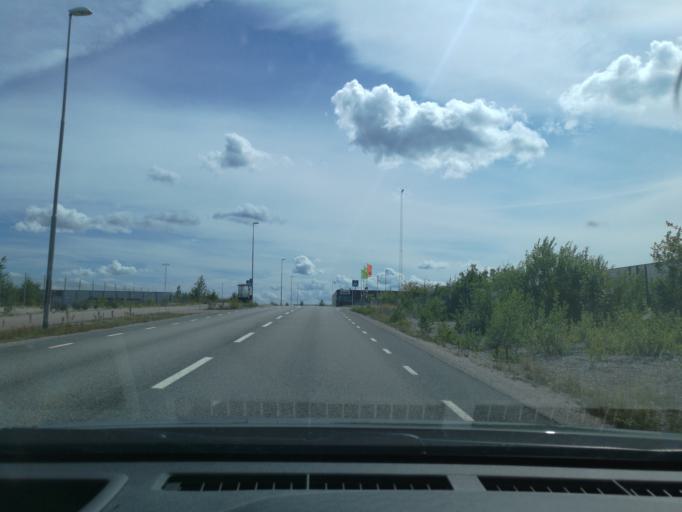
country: SE
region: Stockholm
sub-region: Sigtuna Kommun
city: Rosersberg
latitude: 59.5741
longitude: 17.8754
